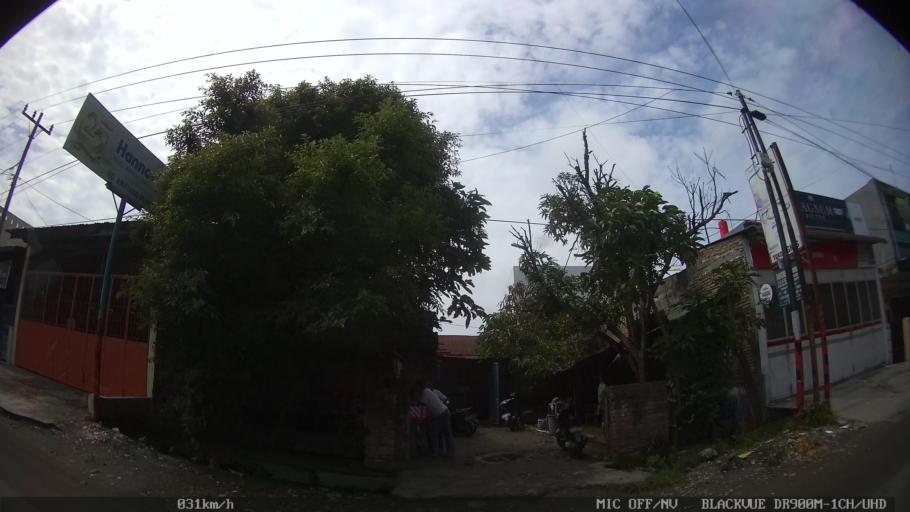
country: ID
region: North Sumatra
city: Medan
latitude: 3.5866
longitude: 98.7303
